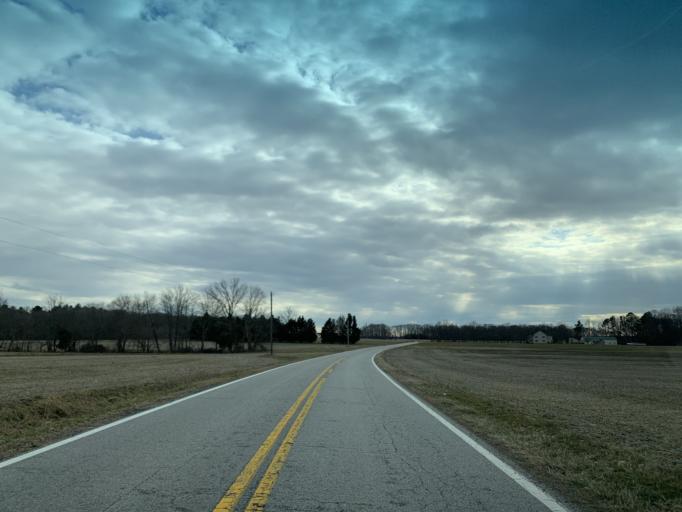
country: US
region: Maryland
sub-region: Caroline County
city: Ridgely
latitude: 38.9694
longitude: -75.9741
